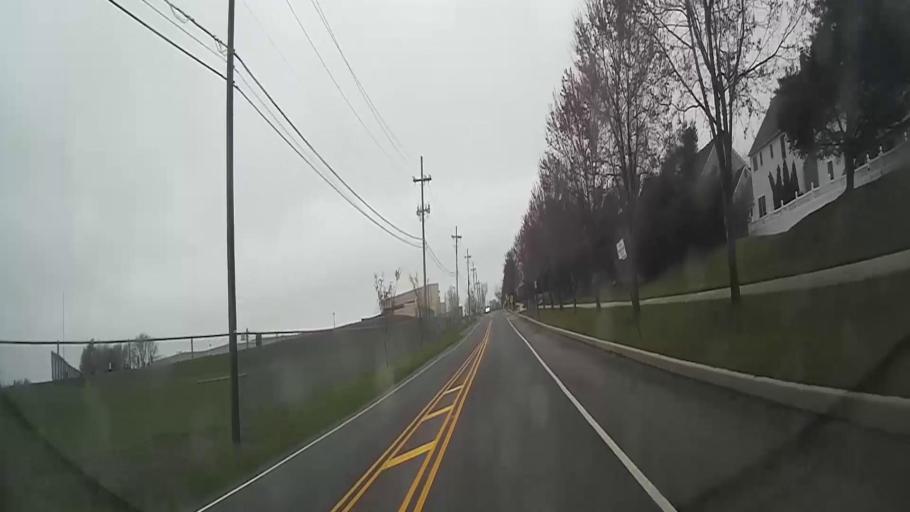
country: US
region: New Jersey
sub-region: Burlington County
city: Marlton
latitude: 39.8717
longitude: -74.8953
